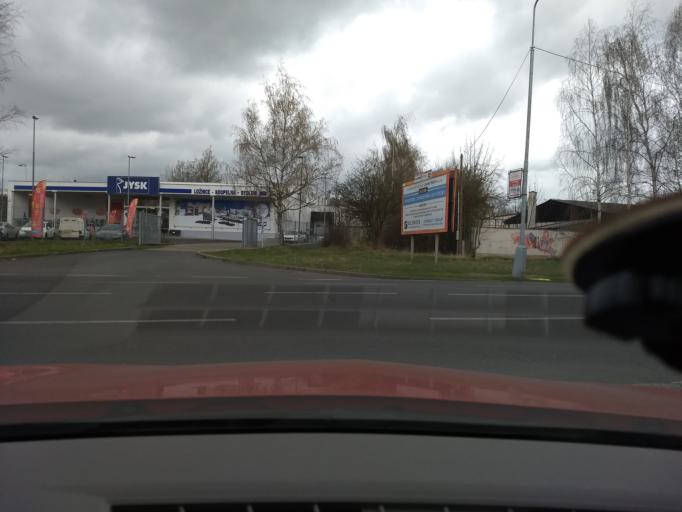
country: CZ
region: Central Bohemia
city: Kladno
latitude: 50.1282
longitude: 14.1178
